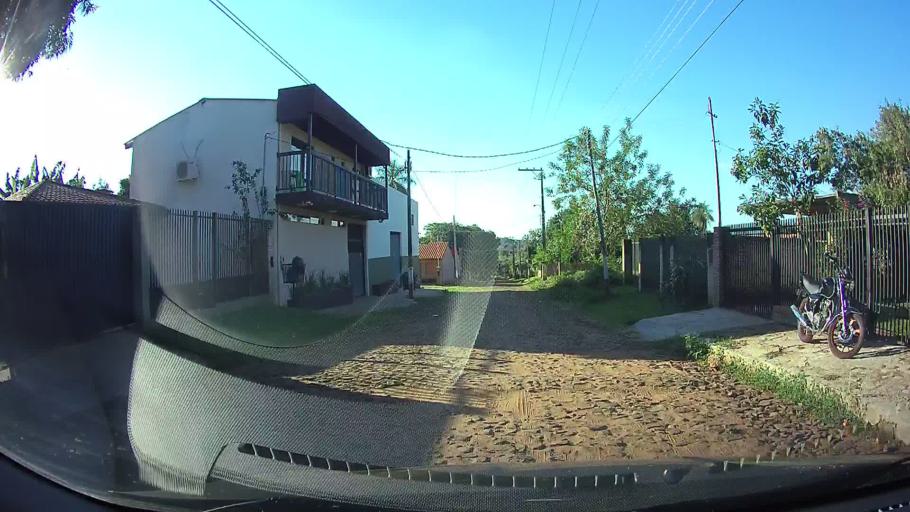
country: PY
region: Central
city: Capiata
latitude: -25.2867
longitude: -57.4594
